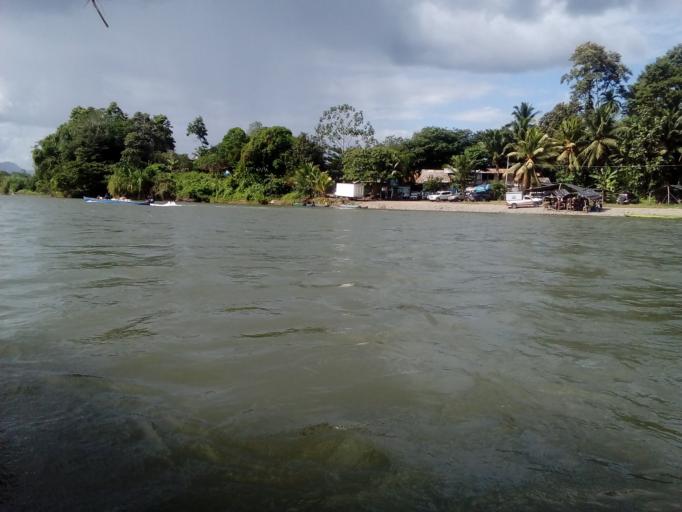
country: PA
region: Bocas del Toro
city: Barranco
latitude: 9.5647
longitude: -82.9361
